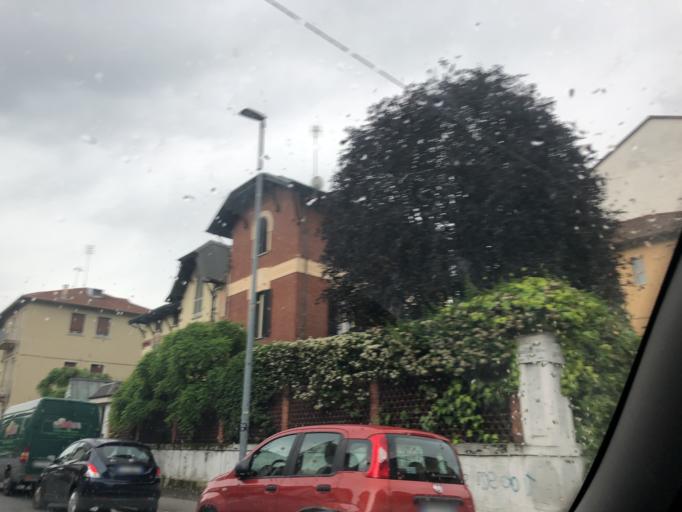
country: IT
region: Piedmont
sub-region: Provincia di Torino
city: Lesna
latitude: 45.0779
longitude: 7.6468
